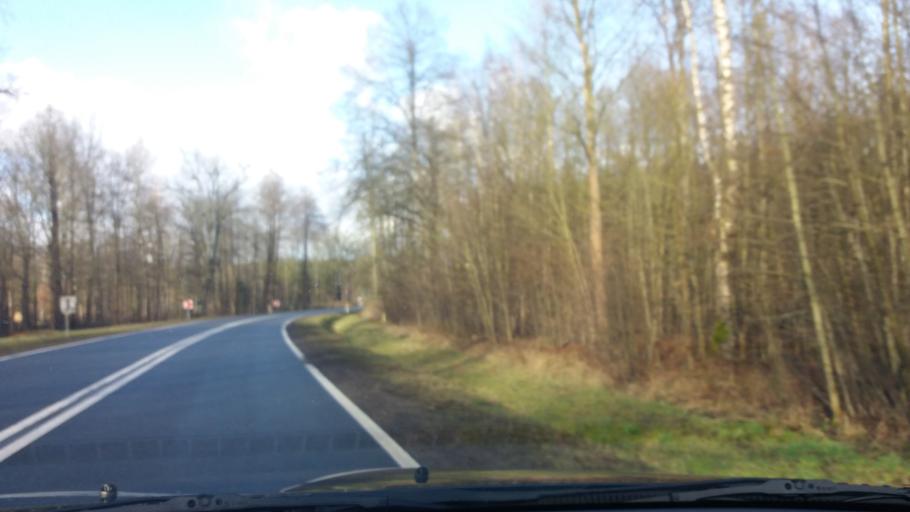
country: PL
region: Masovian Voivodeship
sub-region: Powiat przasnyski
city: Chorzele
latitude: 53.2804
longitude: 20.8985
